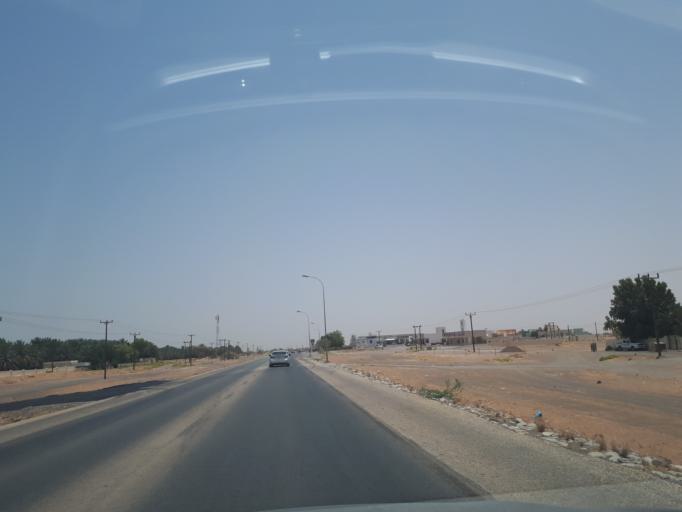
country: OM
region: Ash Sharqiyah
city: Badiyah
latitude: 22.4952
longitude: 58.7558
